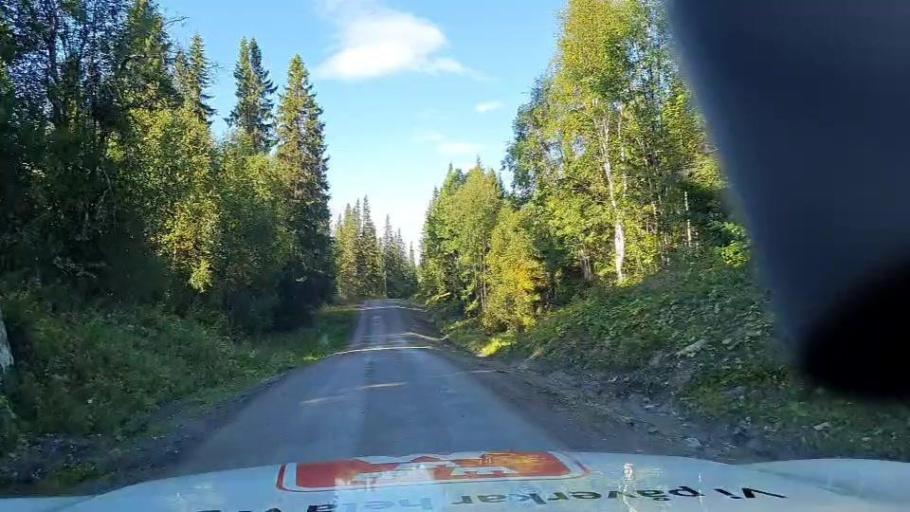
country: SE
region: Jaemtland
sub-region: Stroemsunds Kommun
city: Stroemsund
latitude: 64.5449
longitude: 15.0878
